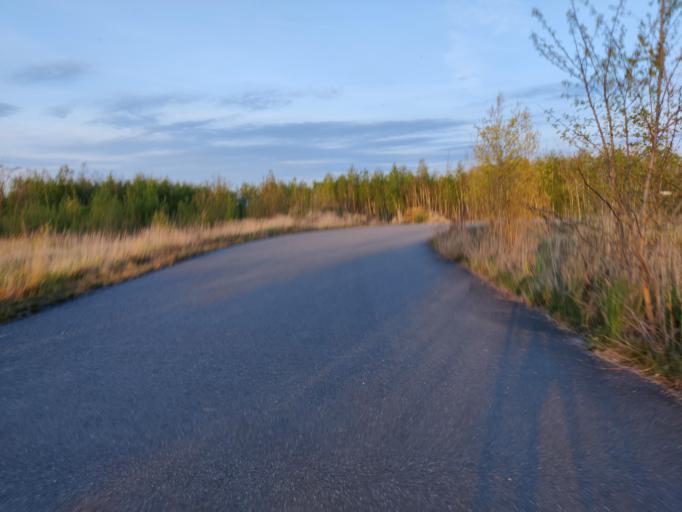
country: DE
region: Saxony
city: Zwenkau
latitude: 51.2147
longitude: 12.3545
